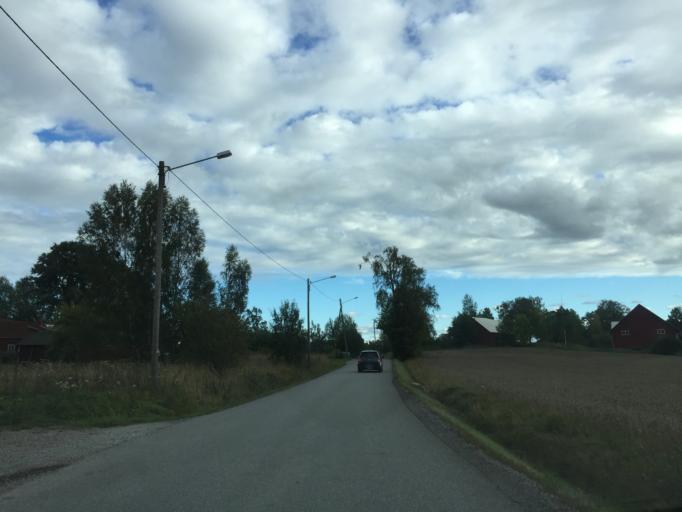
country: SE
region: OErebro
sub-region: Orebro Kommun
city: Hovsta
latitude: 59.3219
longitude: 15.2049
